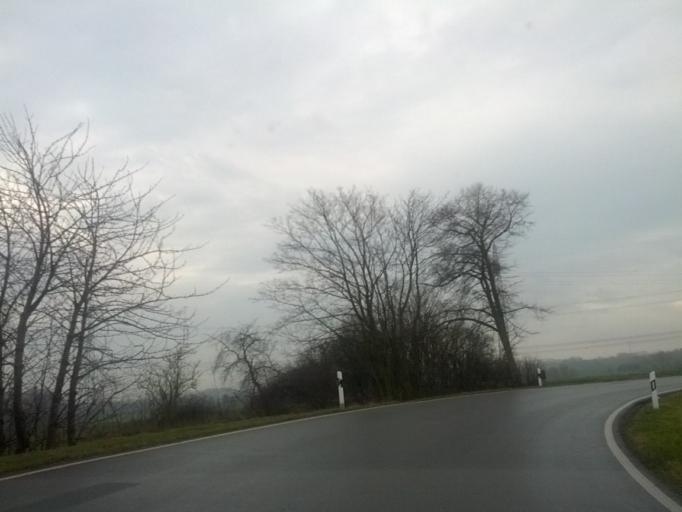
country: DE
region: Thuringia
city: Friedrichswerth
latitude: 50.9806
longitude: 10.5509
